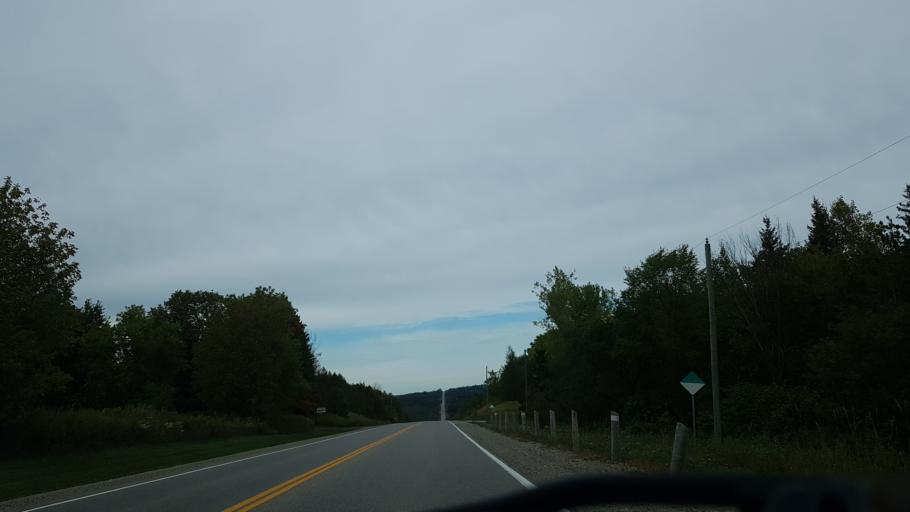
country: CA
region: Ontario
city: Orangeville
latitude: 44.0597
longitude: -80.0137
